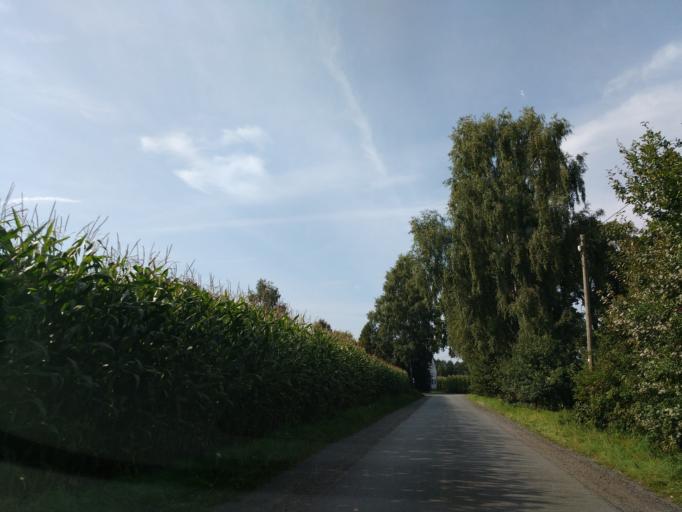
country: DE
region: North Rhine-Westphalia
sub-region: Regierungsbezirk Detmold
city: Delbruck
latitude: 51.7685
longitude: 8.6017
